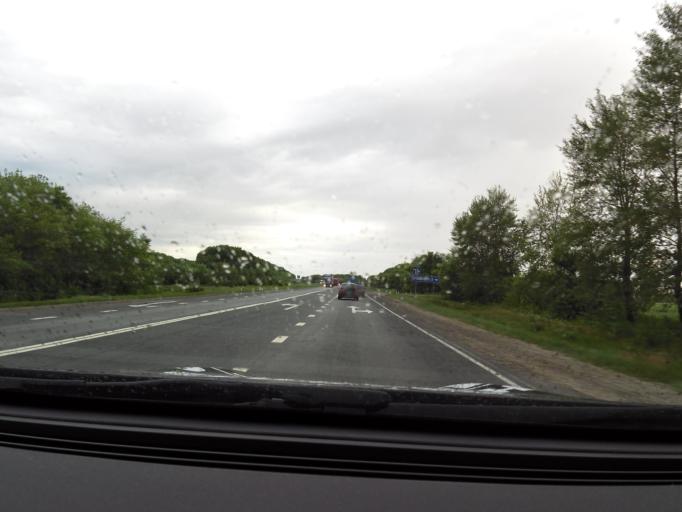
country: RU
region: Chuvashia
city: Yantikovo
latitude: 55.7993
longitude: 47.8541
